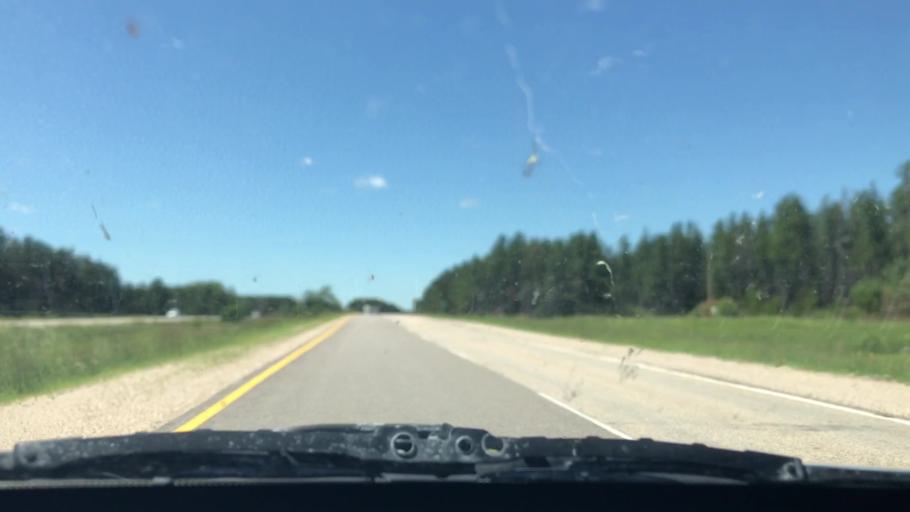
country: CA
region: Manitoba
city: La Broquerie
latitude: 49.6562
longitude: -96.1613
